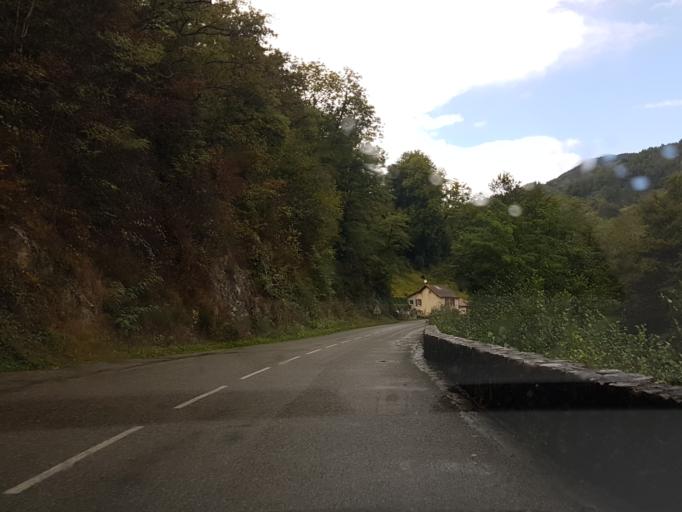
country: FR
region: Midi-Pyrenees
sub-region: Departement de l'Ariege
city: Saint-Girons
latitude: 42.8993
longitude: 1.2308
